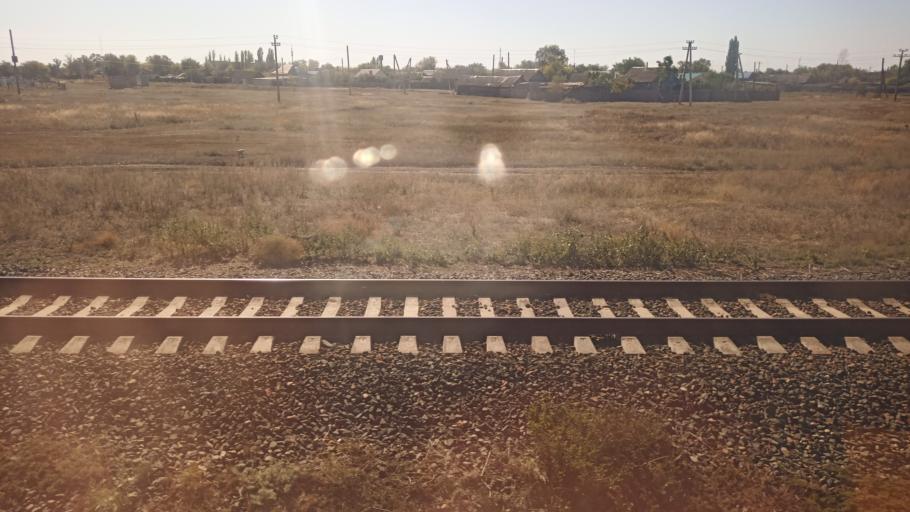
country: RU
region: Saratov
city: Pushkino
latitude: 51.2322
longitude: 46.9849
